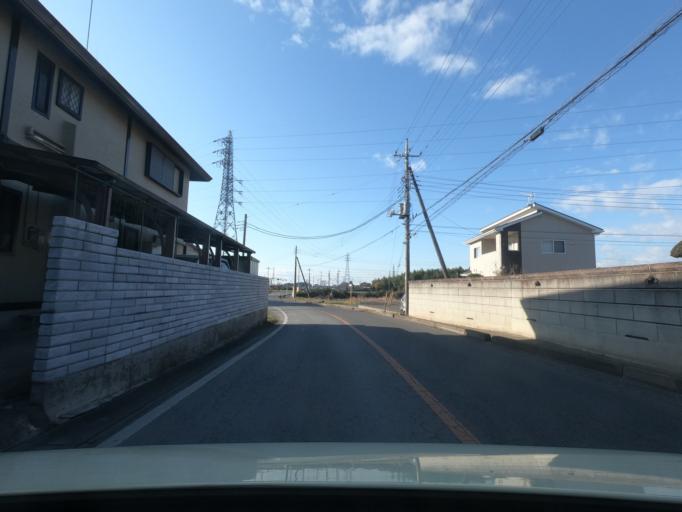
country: JP
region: Ibaraki
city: Koga
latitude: 36.2397
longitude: 139.7464
